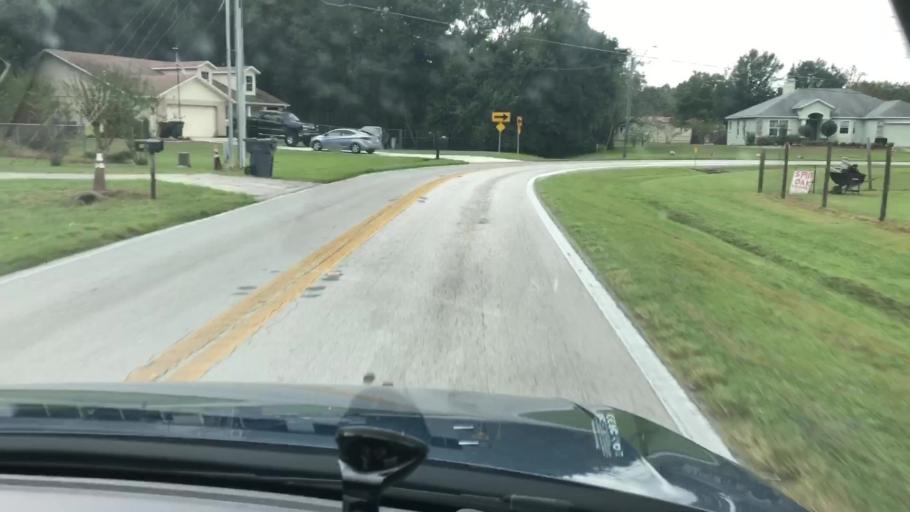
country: US
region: Florida
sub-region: Polk County
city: Kathleen
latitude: 28.1244
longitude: -82.0399
